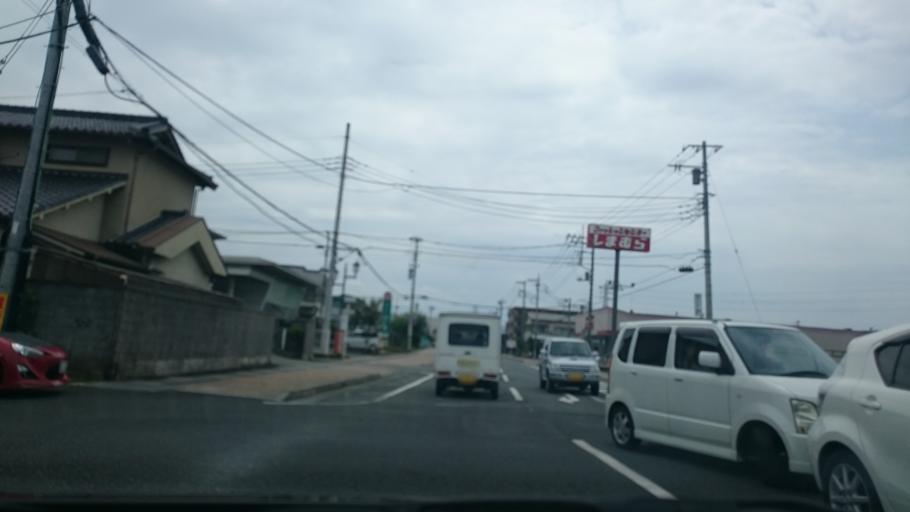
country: JP
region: Shizuoka
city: Mishima
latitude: 35.0853
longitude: 138.9456
